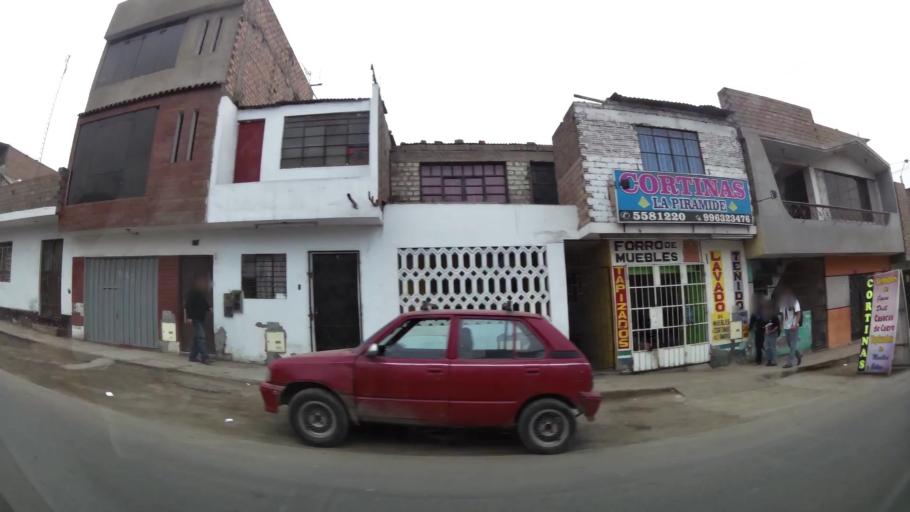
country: PE
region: Lima
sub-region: Lima
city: Urb. Santo Domingo
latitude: -11.9151
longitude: -77.0341
